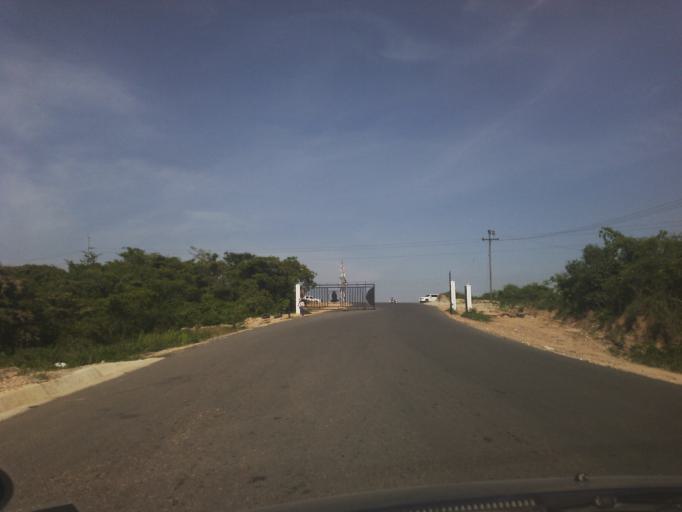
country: TZ
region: Dar es Salaam
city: Magomeni
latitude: -6.7790
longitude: 39.1982
